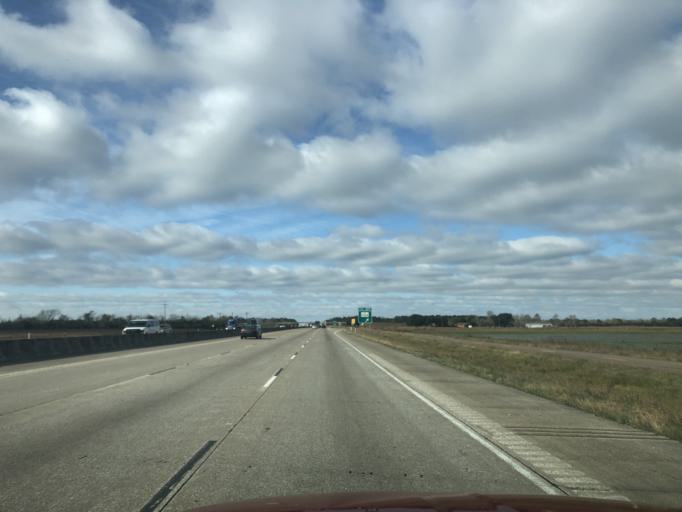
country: US
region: Texas
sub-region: Chambers County
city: Anahuac
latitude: 29.8368
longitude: -94.5691
